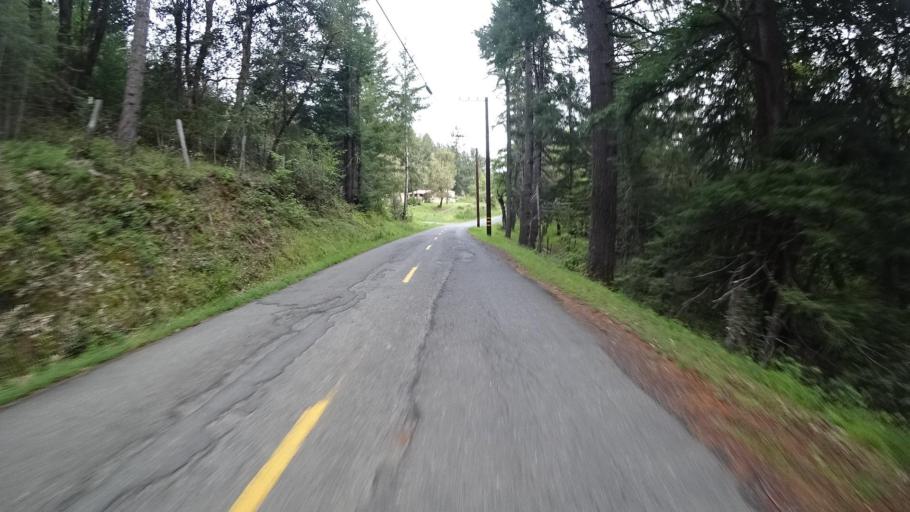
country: US
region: California
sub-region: Humboldt County
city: Redway
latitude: 40.2999
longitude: -123.8219
